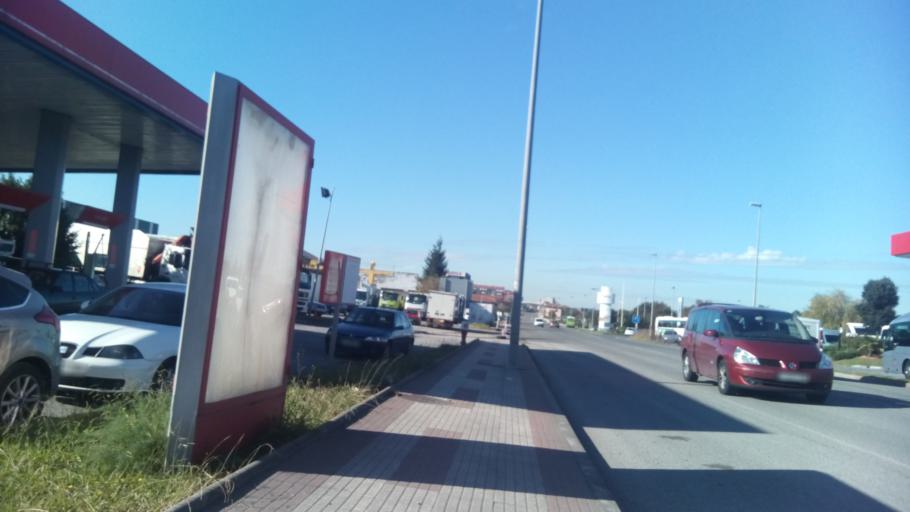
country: ES
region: Basque Country
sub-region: Bizkaia
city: Zamudio
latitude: 43.2798
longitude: -2.8529
